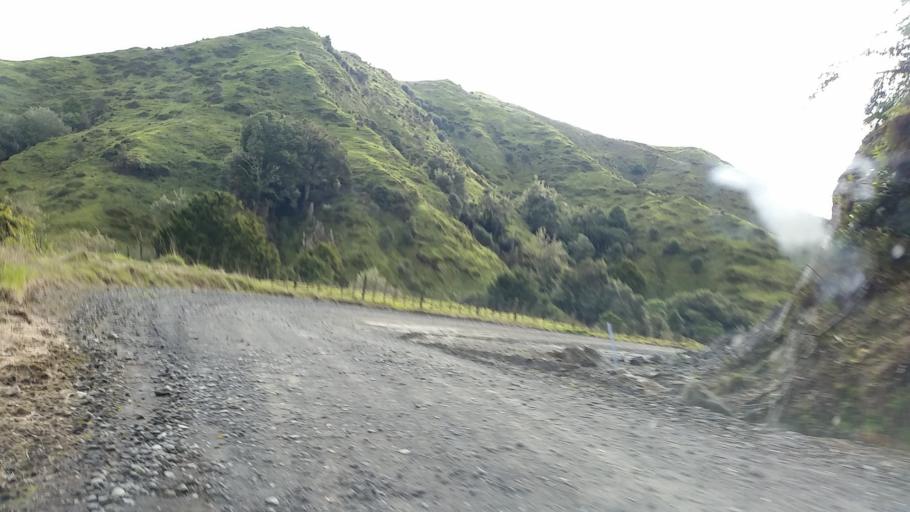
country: NZ
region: Taranaki
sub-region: New Plymouth District
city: Waitara
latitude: -39.1565
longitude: 174.5576
